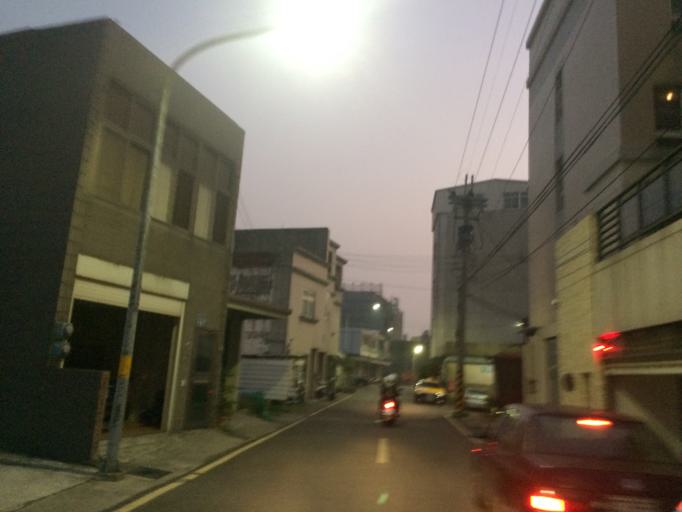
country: TW
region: Taiwan
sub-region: Hsinchu
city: Hsinchu
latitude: 24.7700
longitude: 120.9149
